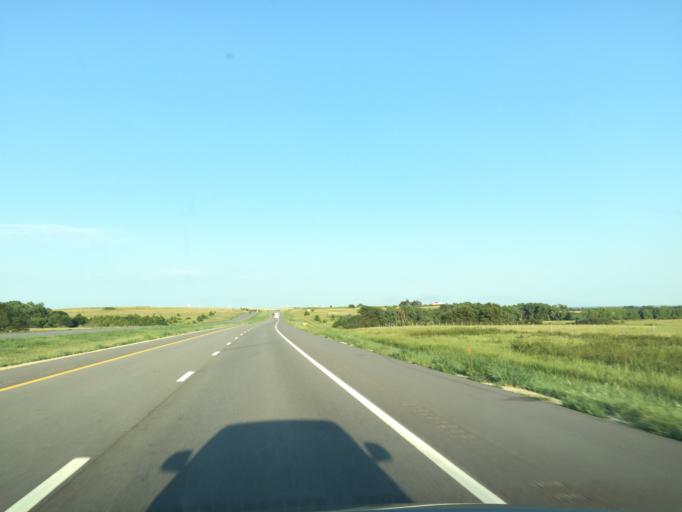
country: US
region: Kansas
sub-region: Ellsworth County
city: Ellsworth
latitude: 38.8548
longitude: -98.5328
